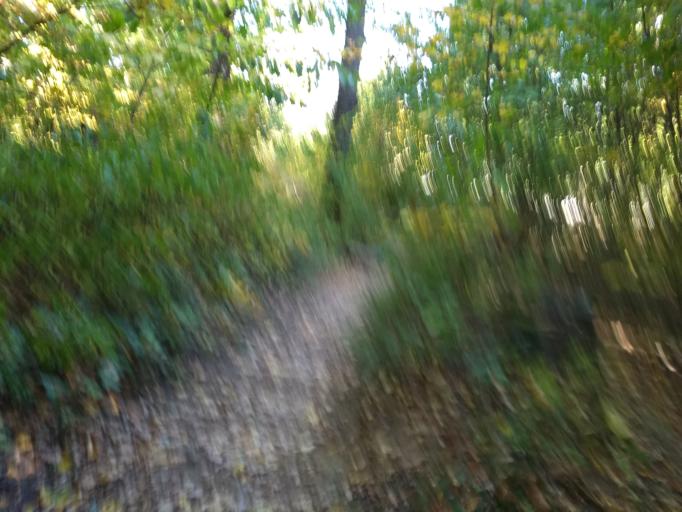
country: AT
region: Lower Austria
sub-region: Politischer Bezirk Modling
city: Giesshubl
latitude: 48.1070
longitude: 16.2406
